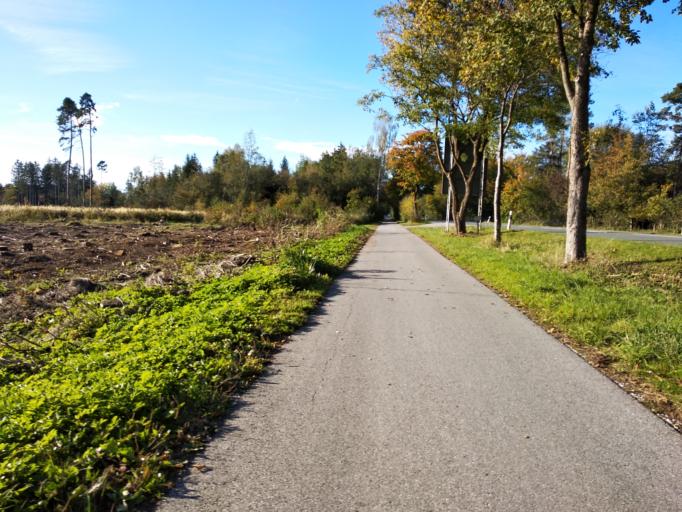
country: DE
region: Bavaria
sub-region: Upper Bavaria
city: Hohenbrunn
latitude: 48.0294
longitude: 11.6935
